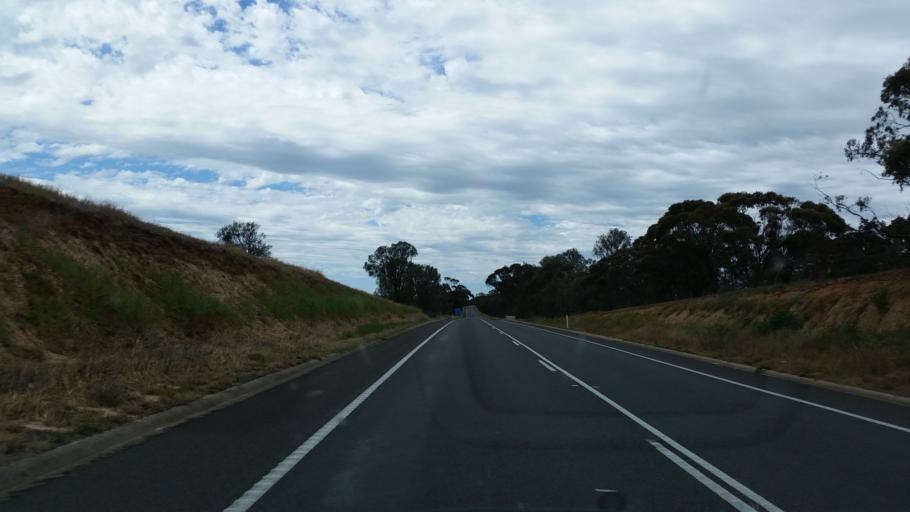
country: AU
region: South Australia
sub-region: Tatiara
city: Bordertown
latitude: -36.3472
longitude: 140.9892
